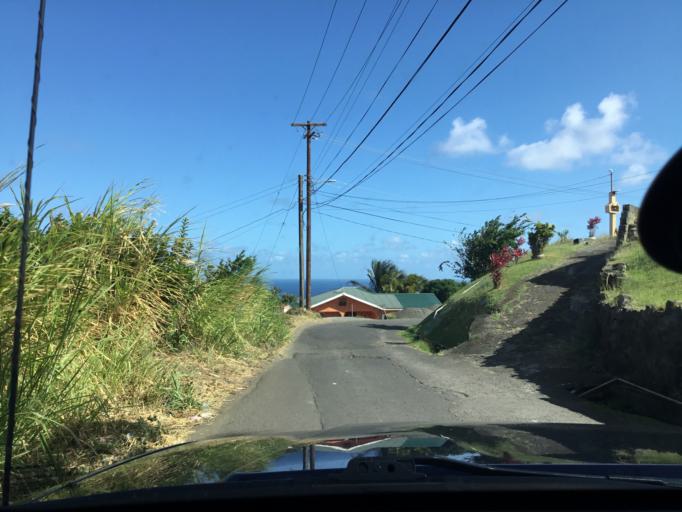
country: VC
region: Charlotte
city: Biabou
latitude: 13.1585
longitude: -61.1579
